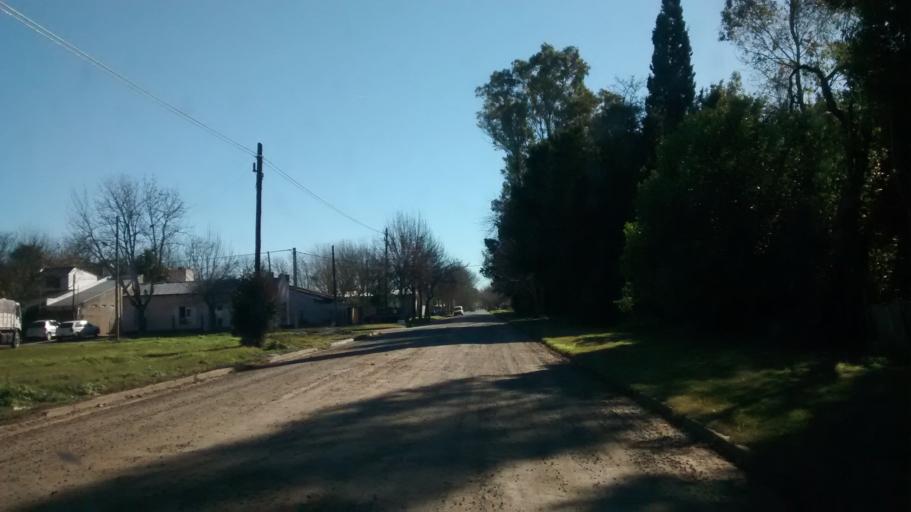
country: AR
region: Buenos Aires
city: Pila
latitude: -36.0027
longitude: -58.1394
